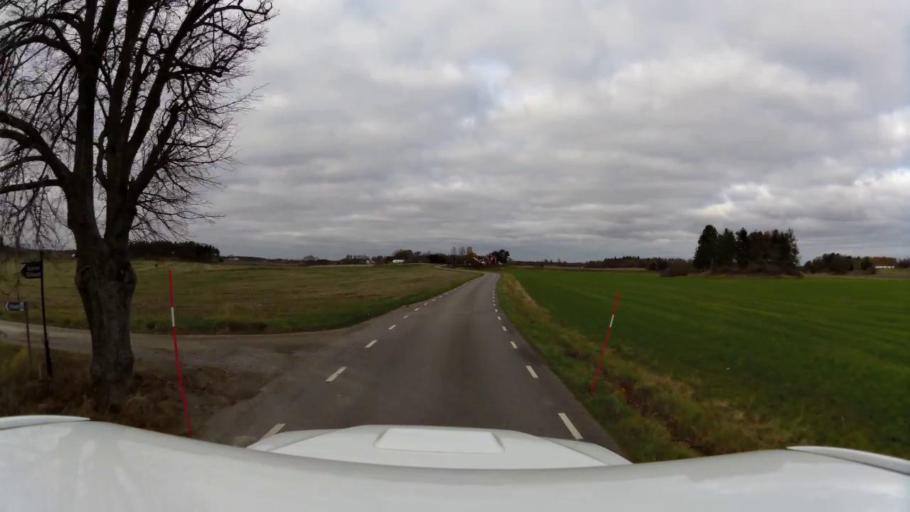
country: SE
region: OEstergoetland
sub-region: Linkopings Kommun
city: Linghem
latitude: 58.3957
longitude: 15.7932
